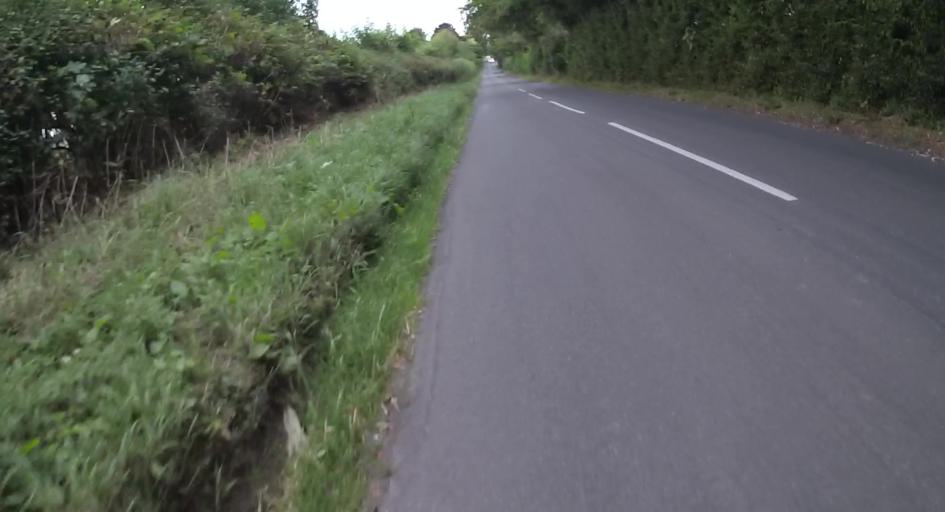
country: GB
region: England
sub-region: Hampshire
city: Kings Worthy
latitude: 51.1334
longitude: -1.3091
